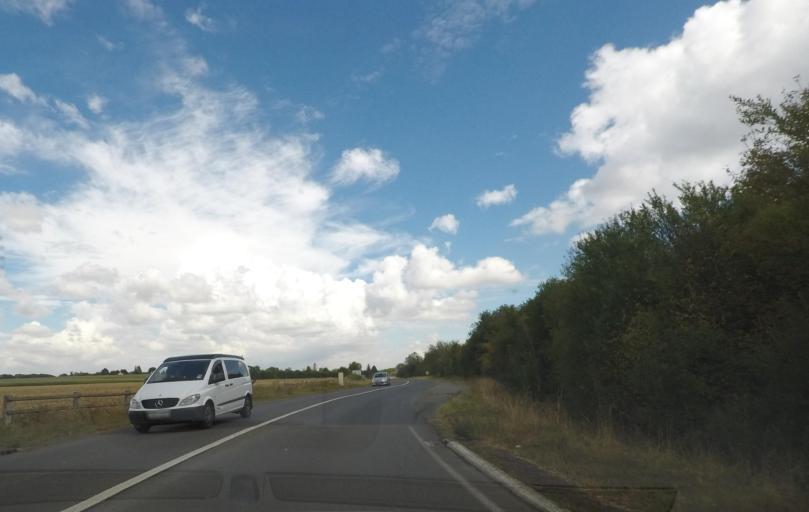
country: FR
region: Pays de la Loire
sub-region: Departement de la Sarthe
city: Champagne
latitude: 48.0813
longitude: 0.3168
